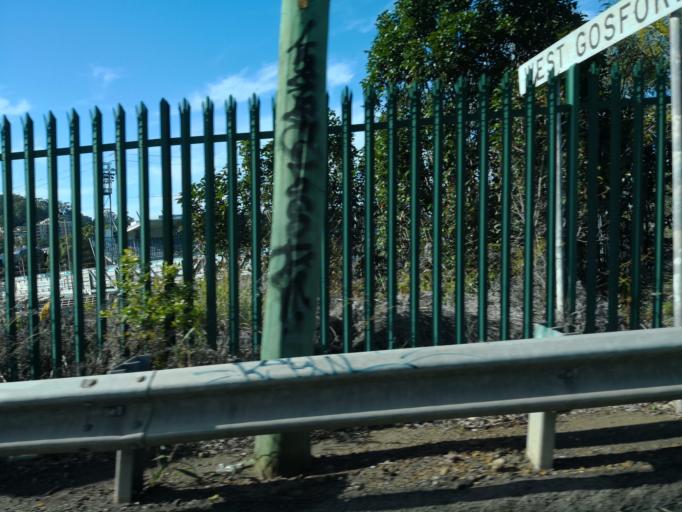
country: AU
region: New South Wales
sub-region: Gosford Shire
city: Gosford
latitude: -33.4271
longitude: 151.3375
